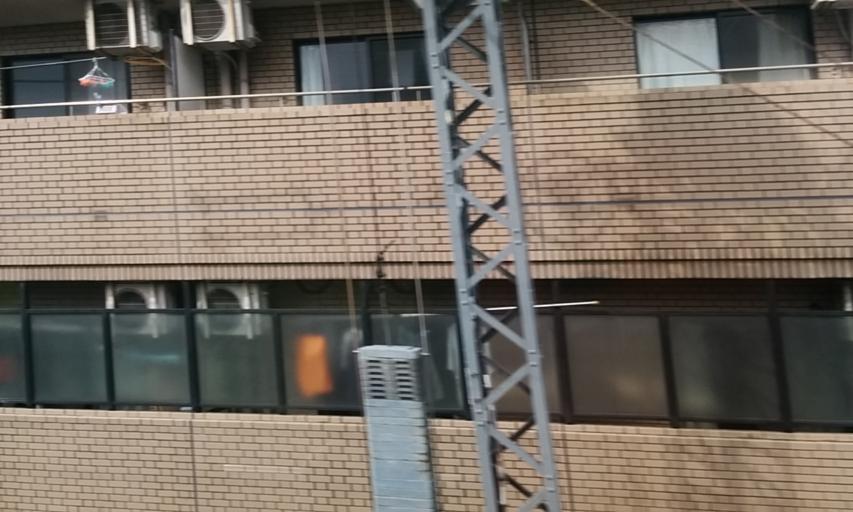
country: JP
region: Nara
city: Tawaramoto
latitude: 34.6088
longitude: 135.7820
